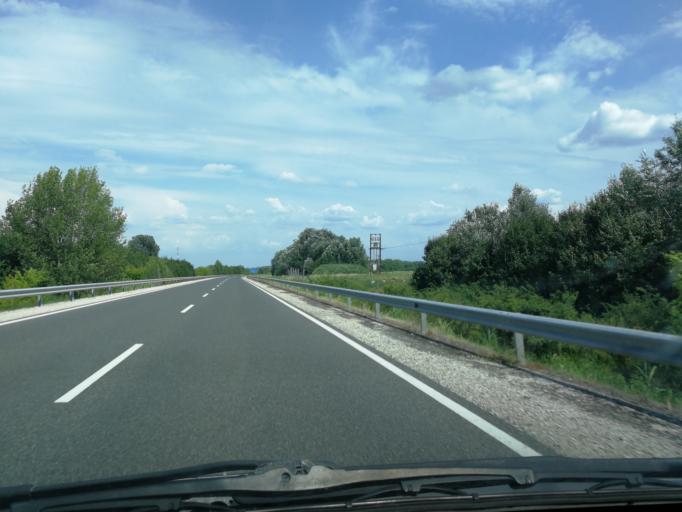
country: HU
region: Tolna
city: Bogyiszlo
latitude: 46.3760
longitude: 18.7930
